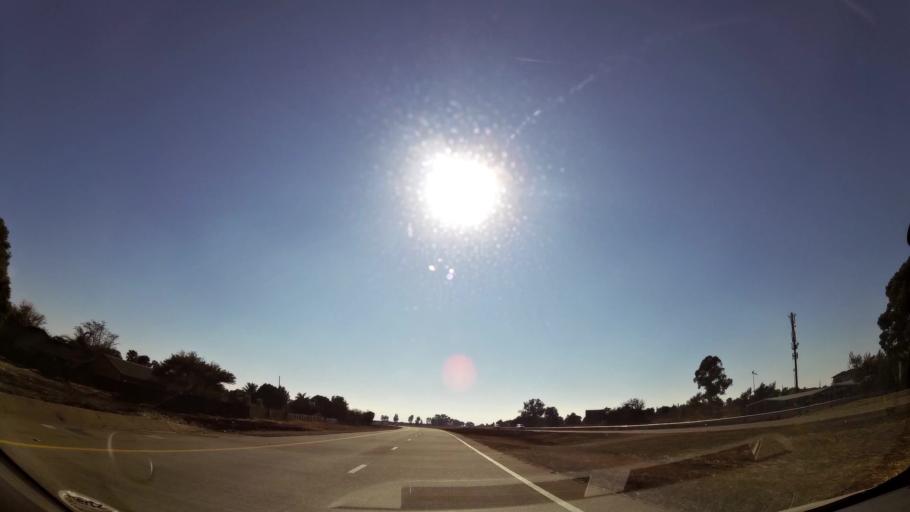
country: ZA
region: Mpumalanga
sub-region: Nkangala District Municipality
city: Witbank
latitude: -25.9019
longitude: 29.2507
